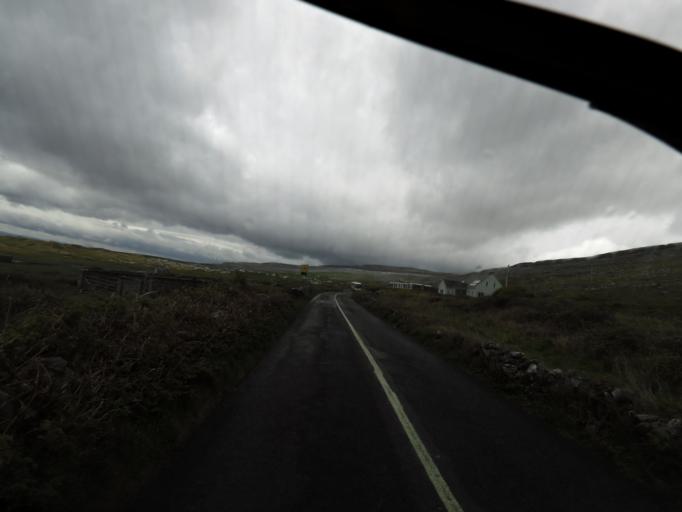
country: IE
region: Connaught
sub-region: County Galway
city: Bearna
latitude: 53.1160
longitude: -9.2858
